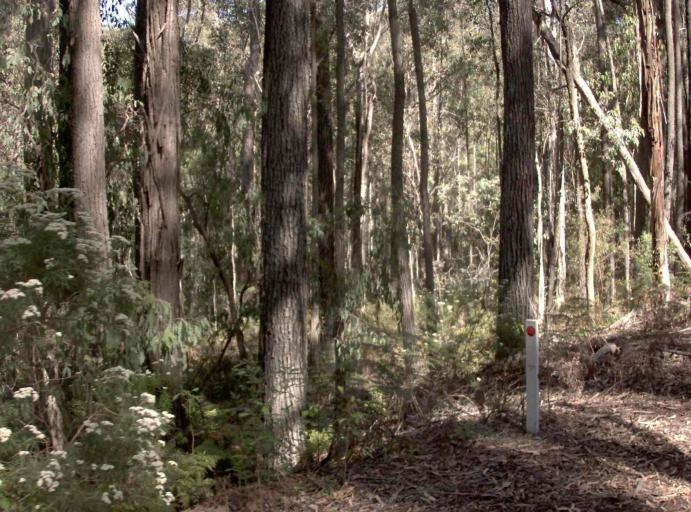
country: AU
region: New South Wales
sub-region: Bombala
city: Bombala
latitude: -37.2847
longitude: 148.7157
